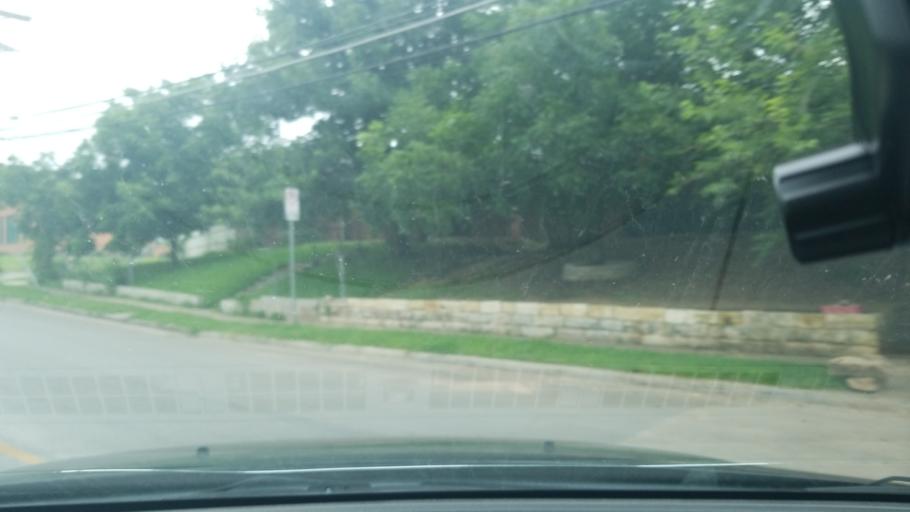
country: US
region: Texas
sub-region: Dallas County
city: Balch Springs
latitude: 32.7582
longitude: -96.6872
